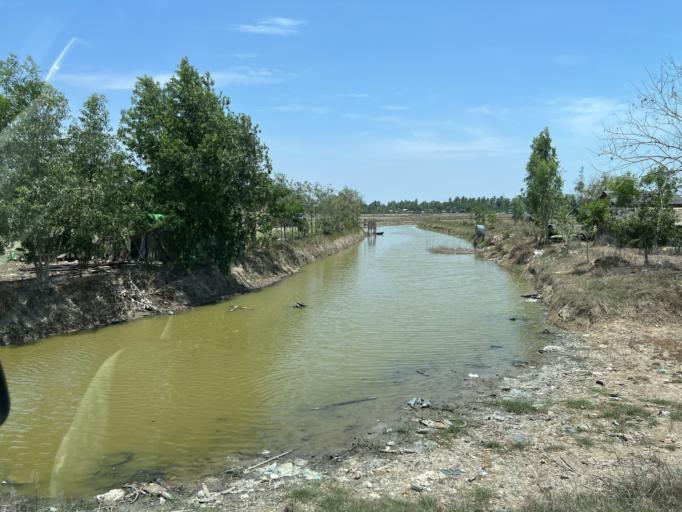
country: MM
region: Ayeyarwady
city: Pyapon
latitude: 15.9138
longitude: 95.6005
